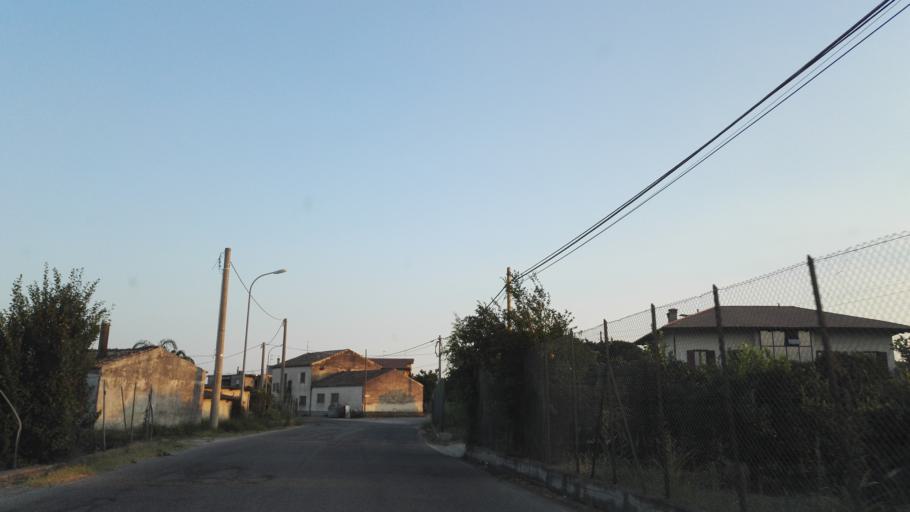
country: IT
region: Calabria
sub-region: Provincia di Reggio Calabria
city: Caulonia Marina
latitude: 38.3557
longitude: 16.4699
